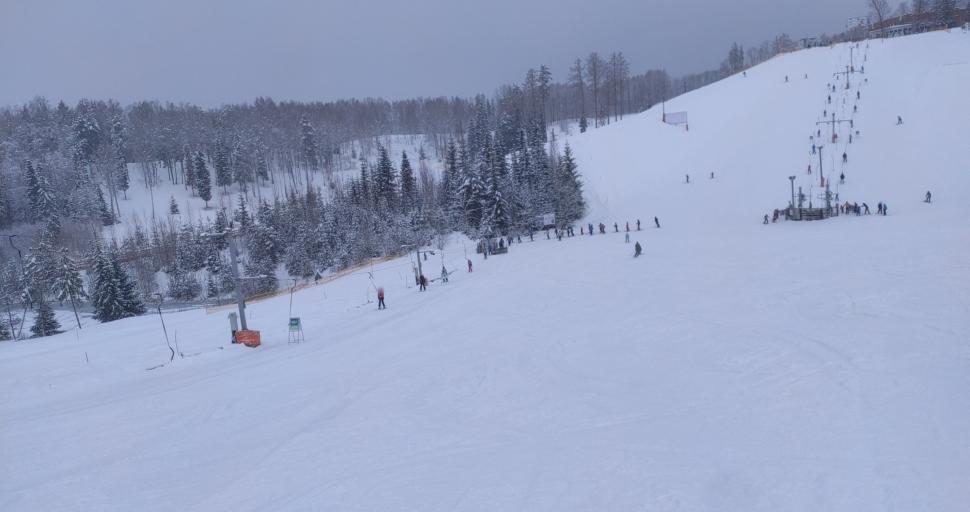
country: LV
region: Cesu Rajons
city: Cesis
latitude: 57.2985
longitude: 25.2279
